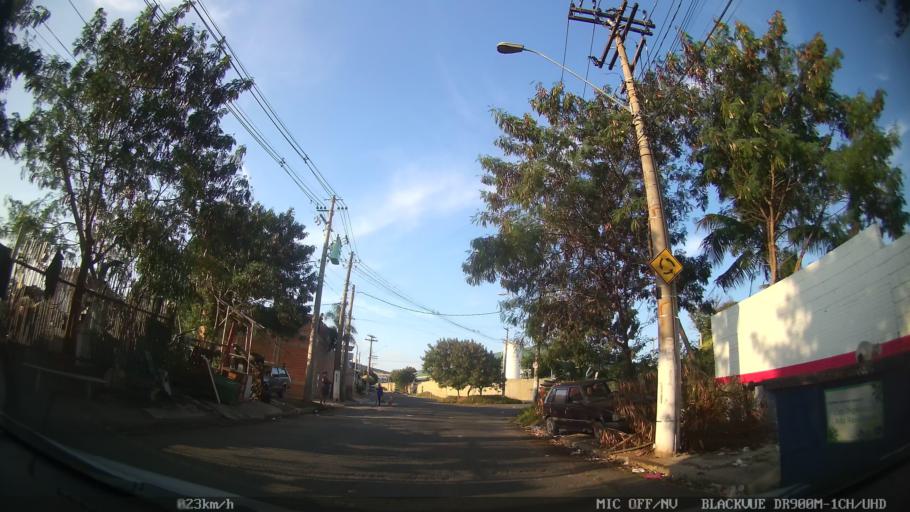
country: BR
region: Sao Paulo
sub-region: Campinas
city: Campinas
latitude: -22.9951
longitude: -47.1176
